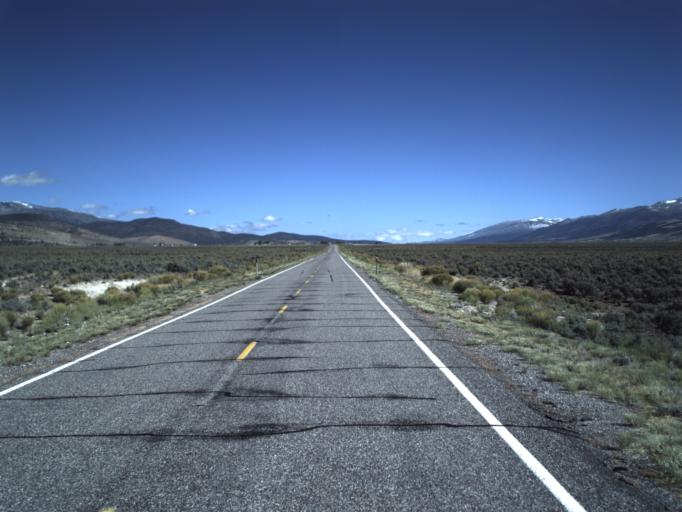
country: US
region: Utah
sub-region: Wayne County
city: Loa
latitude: 38.3997
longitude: -111.9298
